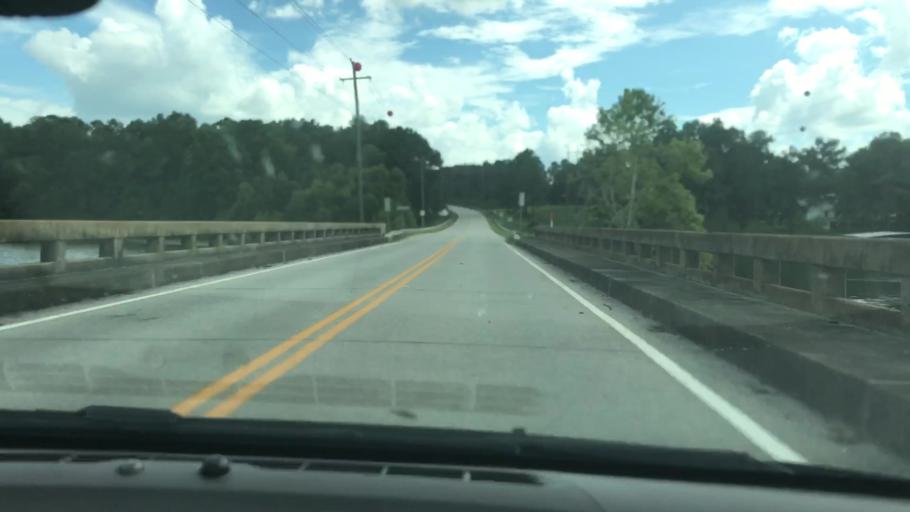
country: US
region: Georgia
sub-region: Clay County
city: Fort Gaines
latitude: 31.7476
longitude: -85.0546
